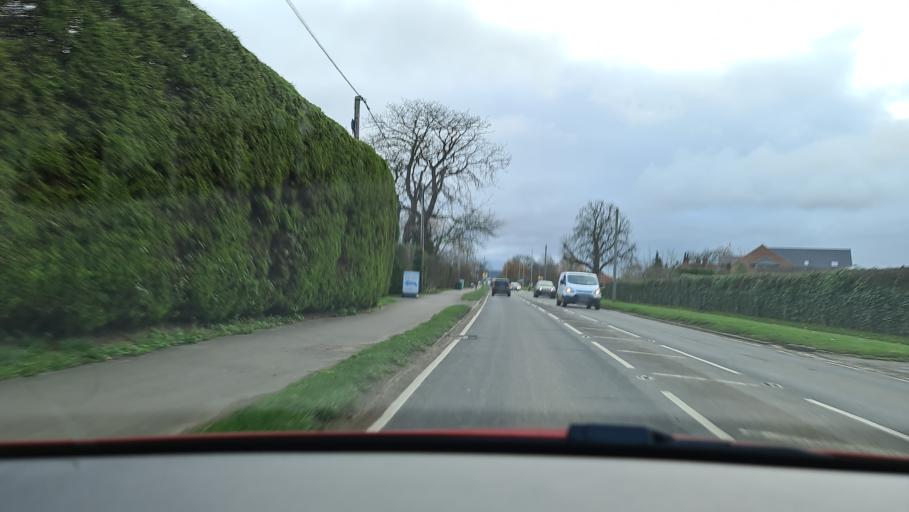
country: GB
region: England
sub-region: Buckinghamshire
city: Aylesbury
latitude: 51.7872
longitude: -0.7955
